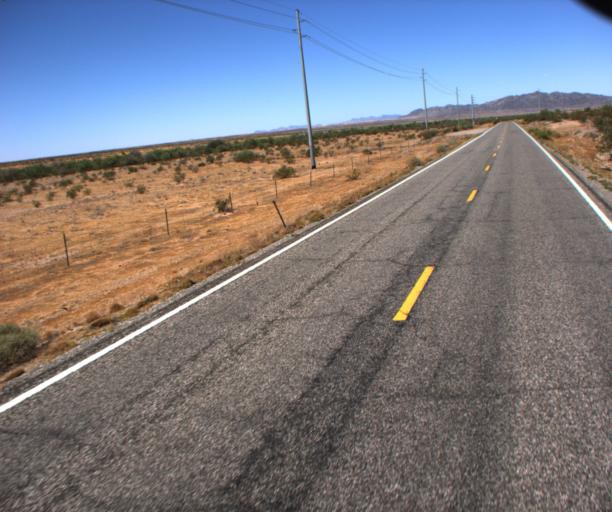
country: US
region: Arizona
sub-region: La Paz County
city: Parker
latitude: 33.9949
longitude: -114.1614
